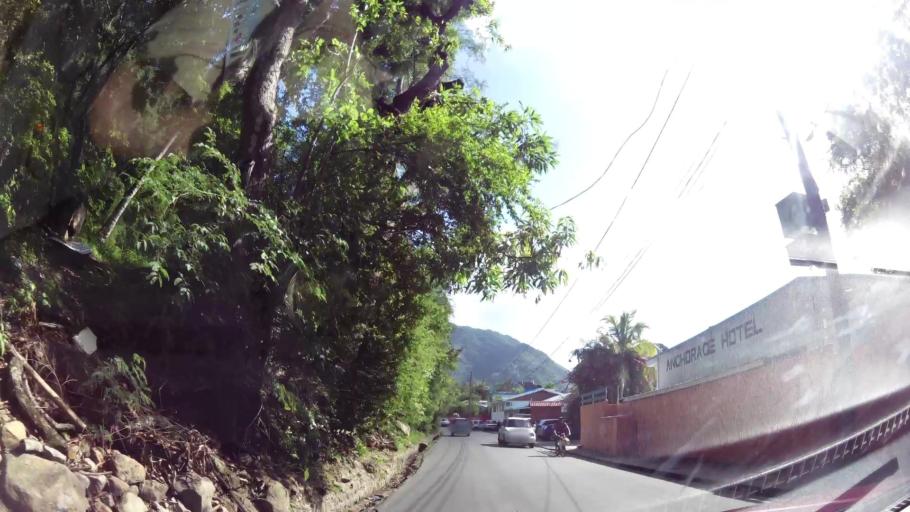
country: DM
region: Saint George
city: Roseau
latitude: 15.2863
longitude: -61.3756
